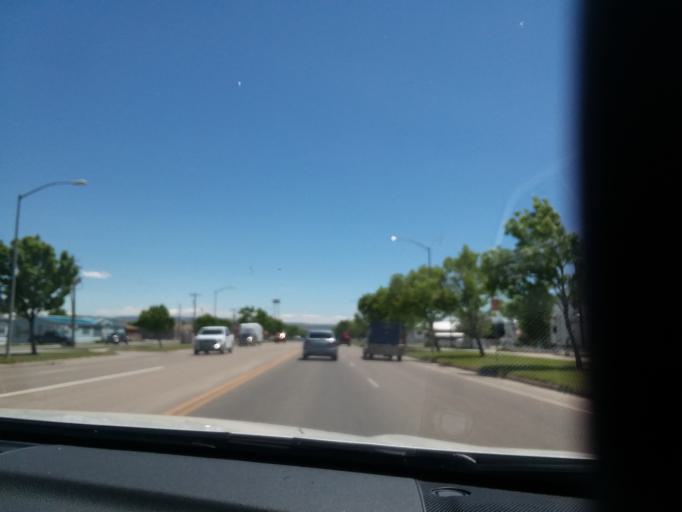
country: US
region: Wyoming
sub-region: Sweetwater County
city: Rock Springs
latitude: 41.6170
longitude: -109.2320
